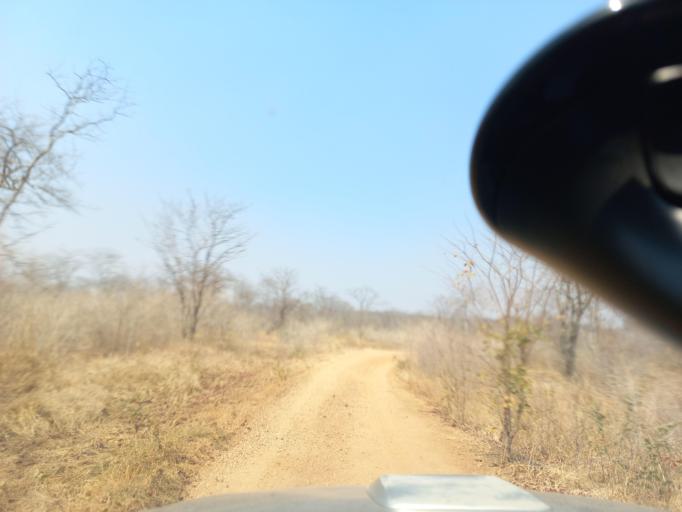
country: ZW
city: Chirundu
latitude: -15.9444
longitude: 28.7555
